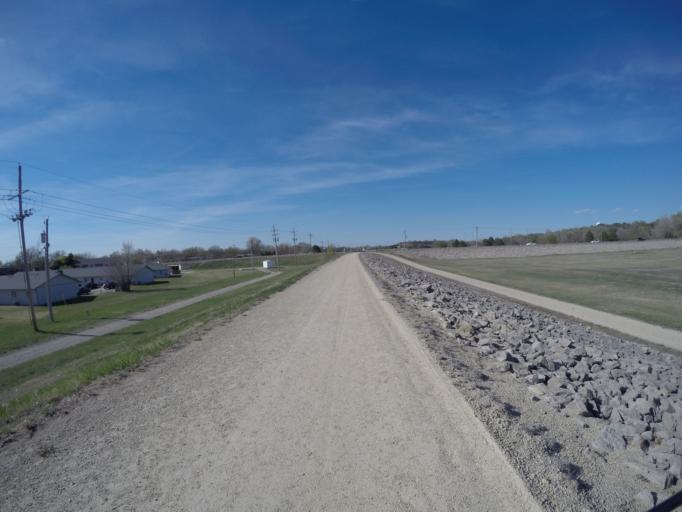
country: US
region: Kansas
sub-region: Saline County
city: Salina
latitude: 38.8259
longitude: -97.5883
